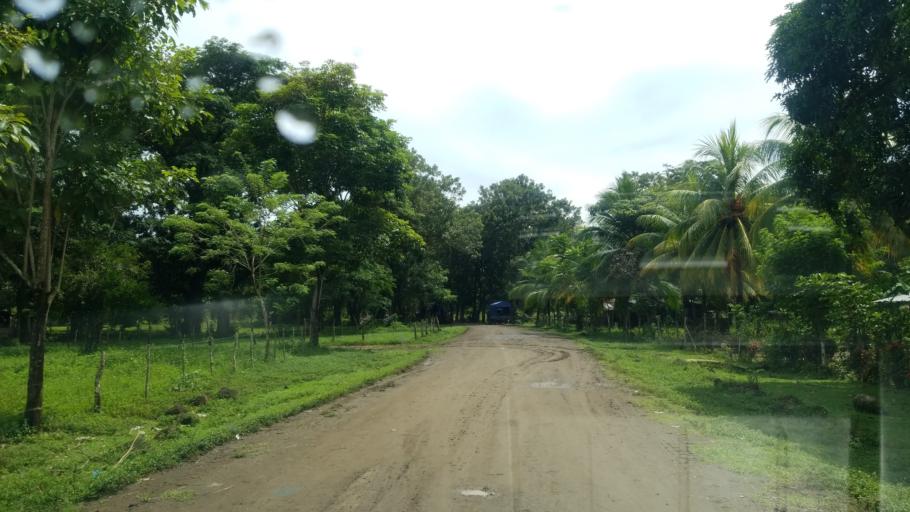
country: CR
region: Alajuela
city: San Jose
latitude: 11.0934
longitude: -85.2295
